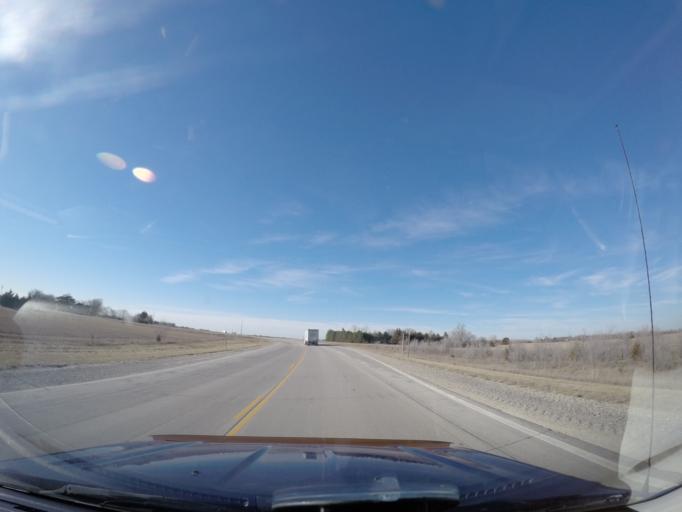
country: US
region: Kansas
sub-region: Marion County
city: Hillsboro
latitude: 38.3613
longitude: -97.1112
